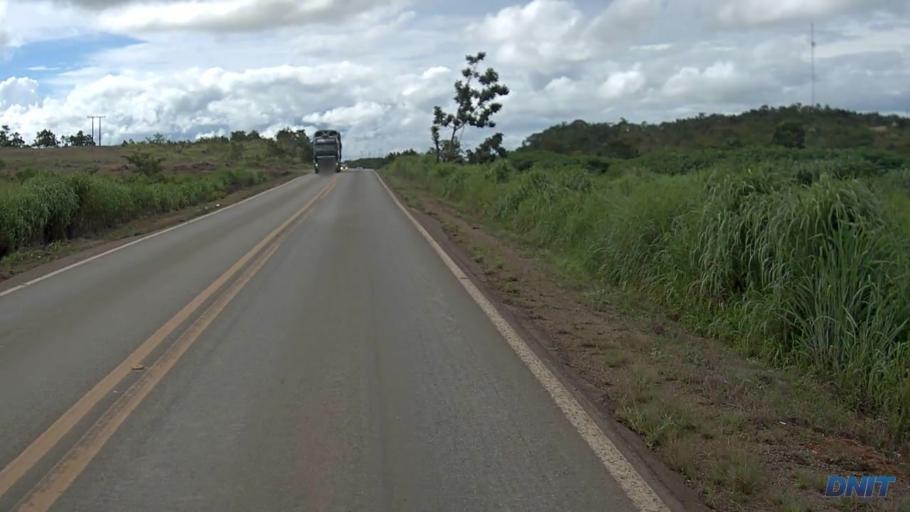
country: BR
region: Goias
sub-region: Padre Bernardo
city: Padre Bernardo
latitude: -15.2264
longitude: -48.2780
